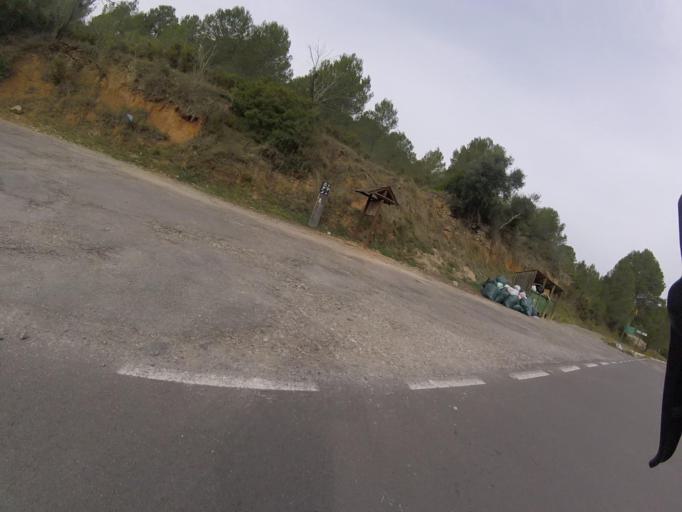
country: ES
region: Valencia
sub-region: Provincia de Castello
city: Cabanes
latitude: 40.1167
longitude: 0.0478
